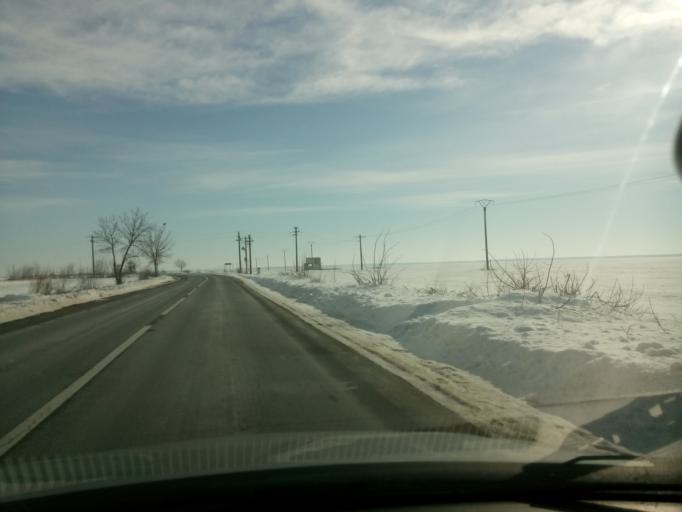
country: RO
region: Giurgiu
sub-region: Comuna Herasti
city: Herasti
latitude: 44.2493
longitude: 26.3715
